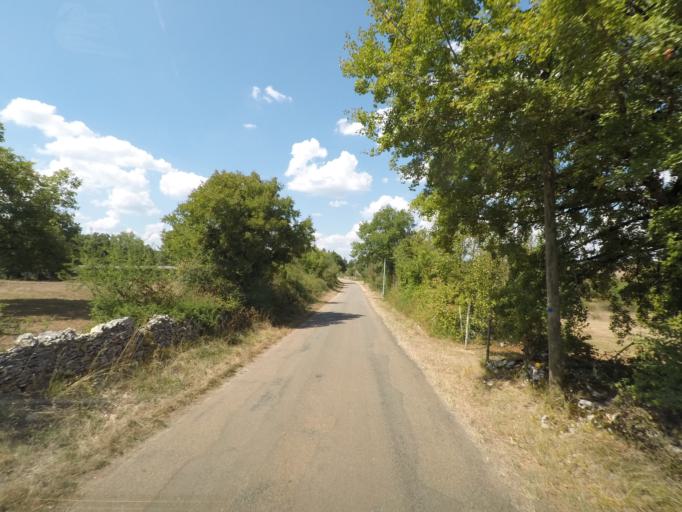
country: FR
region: Midi-Pyrenees
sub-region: Departement du Lot
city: Lalbenque
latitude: 44.5224
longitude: 1.6246
